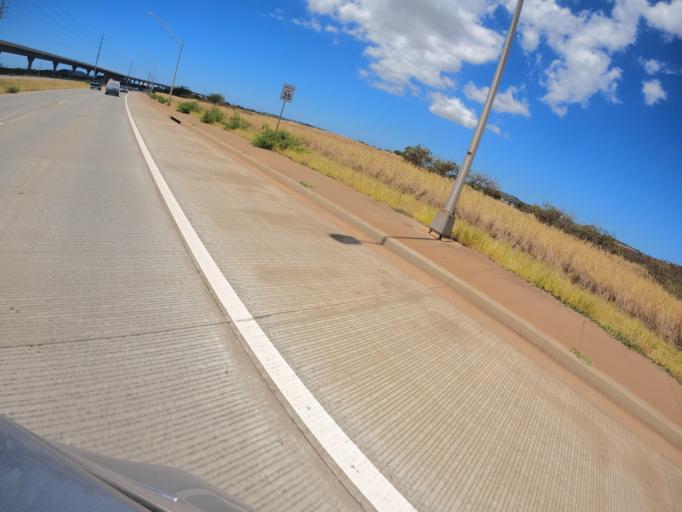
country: US
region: Hawaii
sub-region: Honolulu County
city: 'Ewa Villages
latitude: 21.3511
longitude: -158.0490
